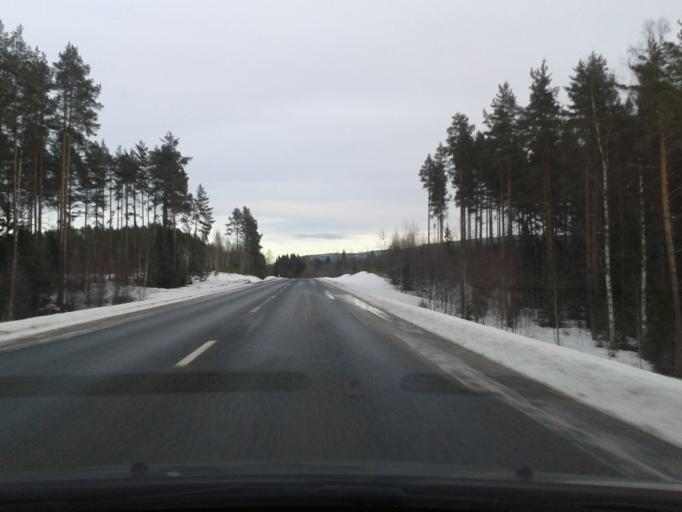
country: SE
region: Vaesternorrland
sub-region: Solleftea Kommun
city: Solleftea
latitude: 63.3389
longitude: 17.0781
